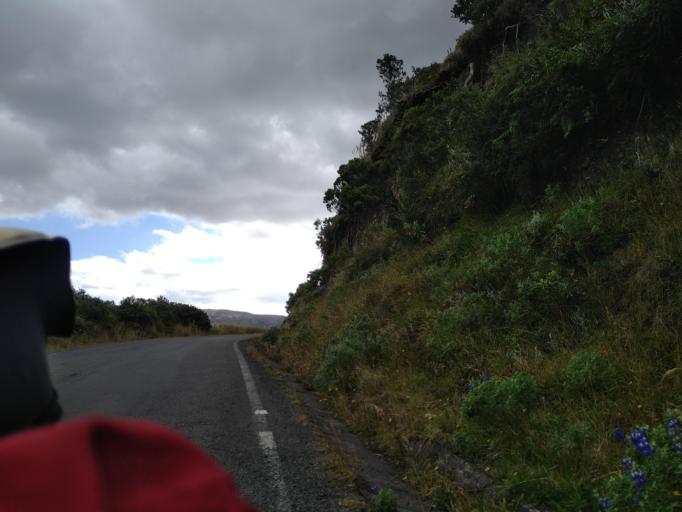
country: EC
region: Cotopaxi
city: Saquisili
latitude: -0.7120
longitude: -78.7630
